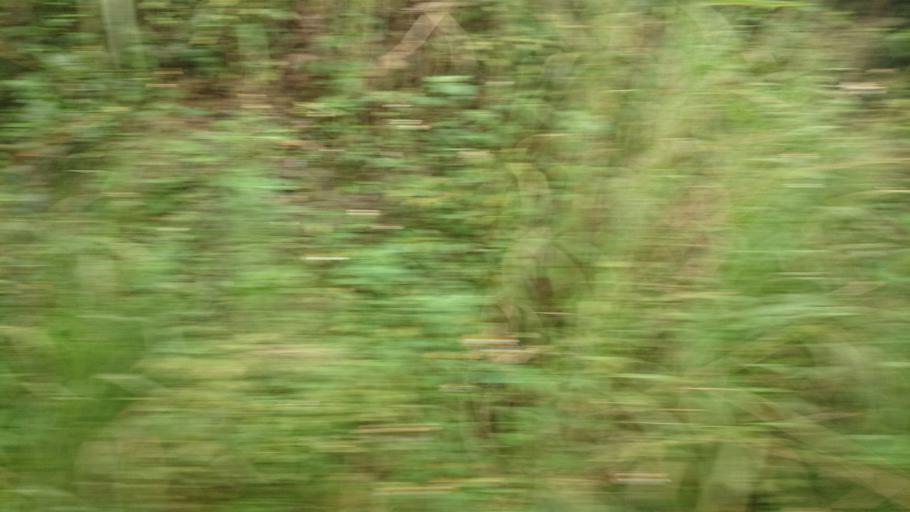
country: TW
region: Taiwan
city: Lugu
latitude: 23.8256
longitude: 120.8574
